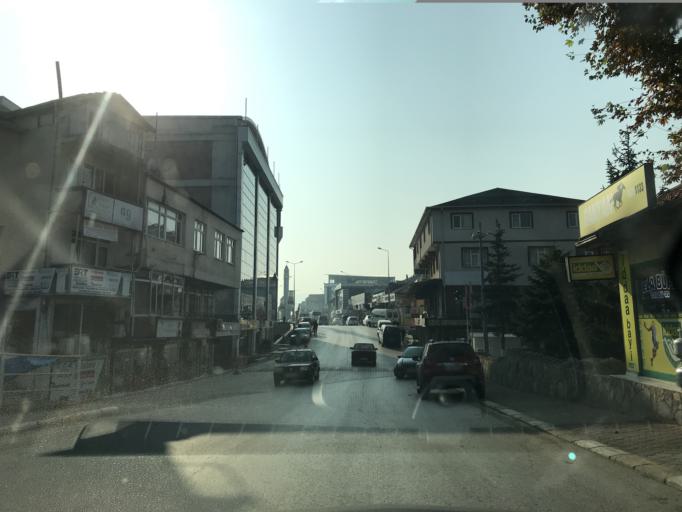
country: TR
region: Duzce
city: Cumayeri
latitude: 40.8750
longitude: 30.9503
